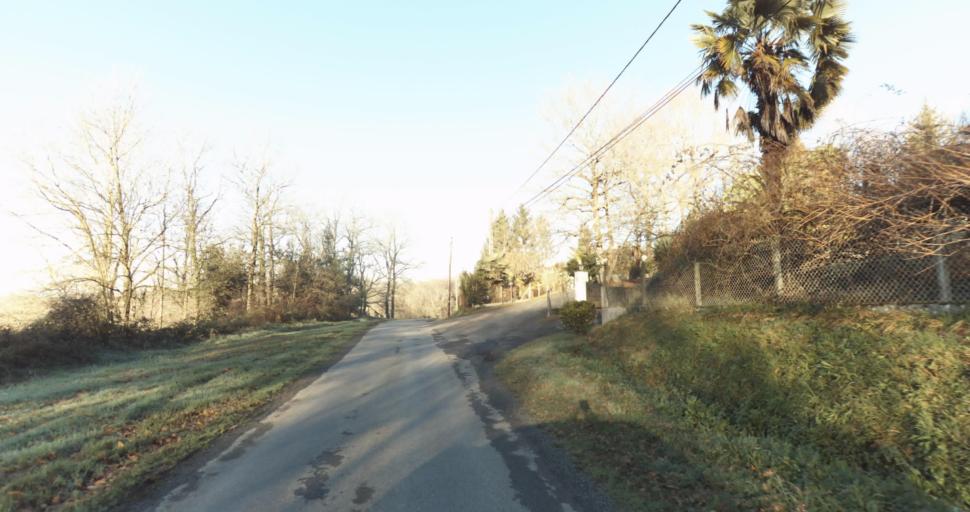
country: FR
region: Aquitaine
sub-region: Departement des Pyrenees-Atlantiques
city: Ousse
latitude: 43.3121
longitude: -0.2444
